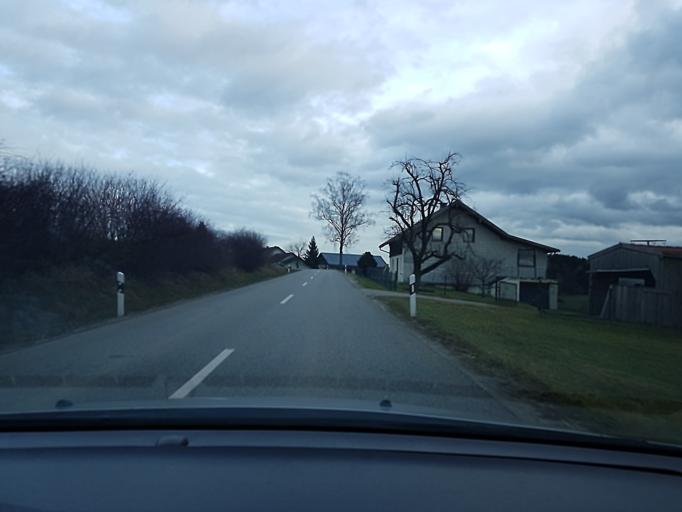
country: DE
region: Bavaria
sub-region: Upper Bavaria
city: Egglkofen
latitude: 48.3978
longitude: 12.4254
